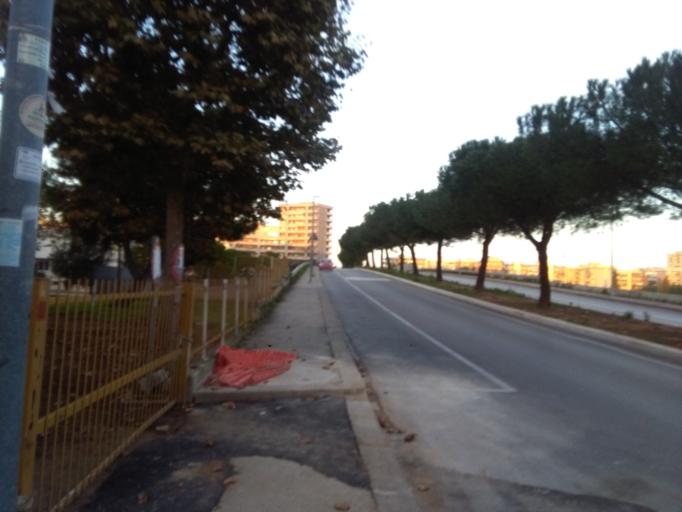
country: IT
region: Apulia
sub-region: Provincia di Bari
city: Bari
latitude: 41.0930
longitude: 16.8596
